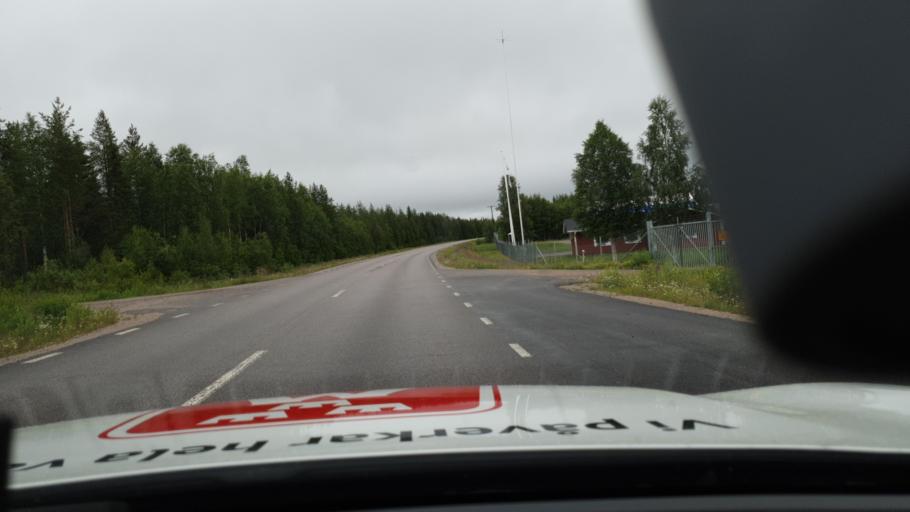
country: SE
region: Norrbotten
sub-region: Overtornea Kommun
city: OEvertornea
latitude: 66.3984
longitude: 23.5611
